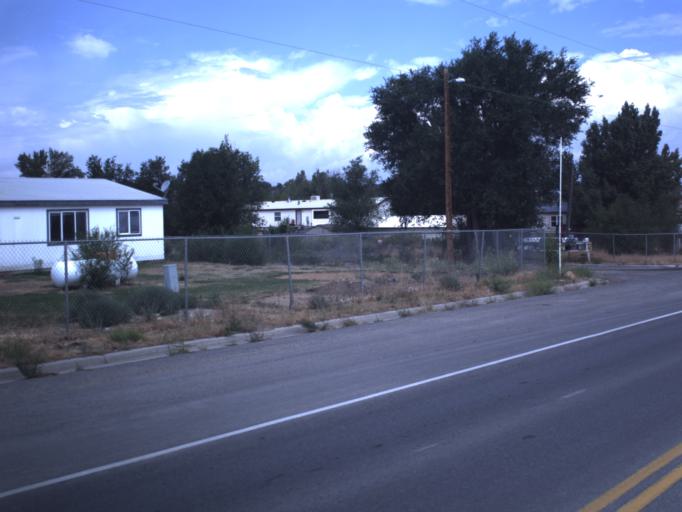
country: US
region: Utah
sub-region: Uintah County
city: Naples
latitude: 40.3696
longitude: -109.4983
